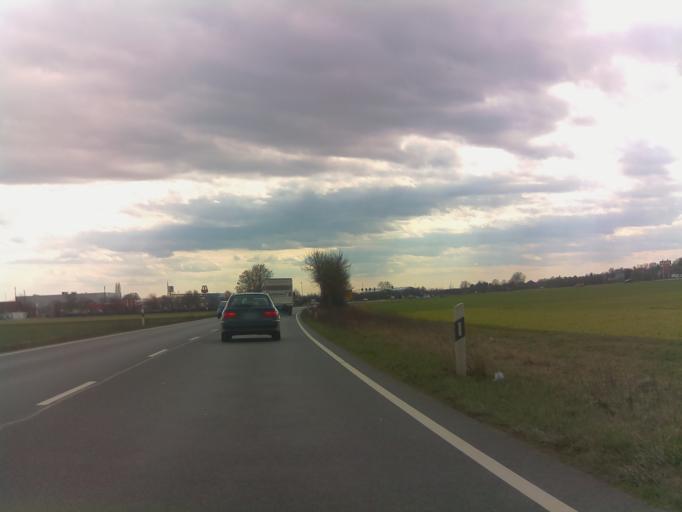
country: DE
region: Hesse
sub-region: Regierungsbezirk Darmstadt
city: Riedstadt
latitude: 49.8401
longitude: 8.4821
